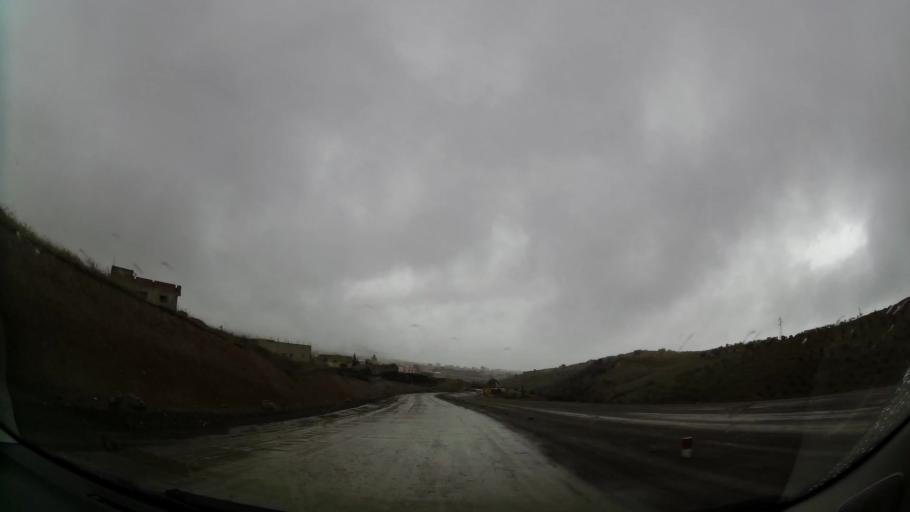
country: MA
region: Oriental
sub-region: Nador
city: Midar
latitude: 34.8887
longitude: -3.7526
